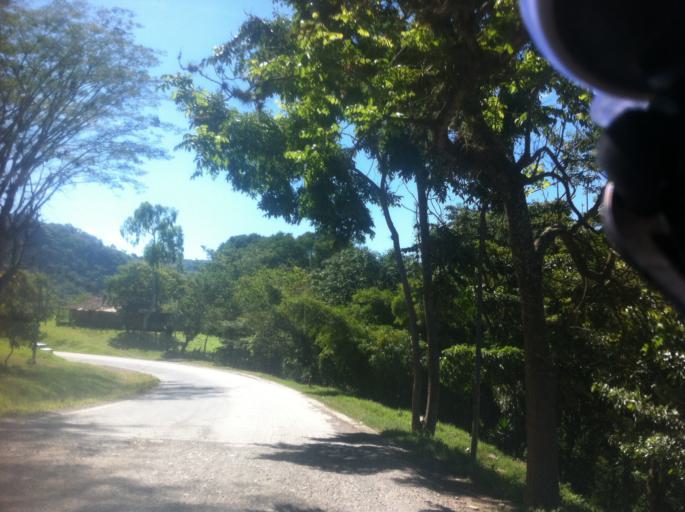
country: NI
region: Matagalpa
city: San Ramon
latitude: 12.9347
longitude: -85.8587
